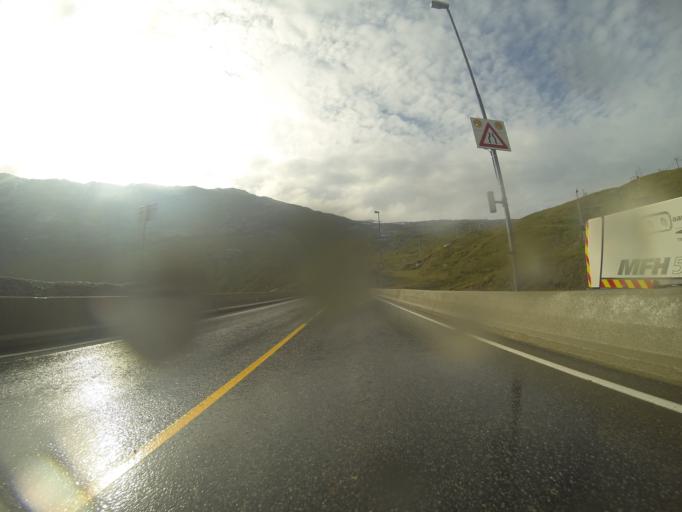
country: NO
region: Hordaland
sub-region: Odda
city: Odda
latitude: 59.8228
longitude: 6.7397
